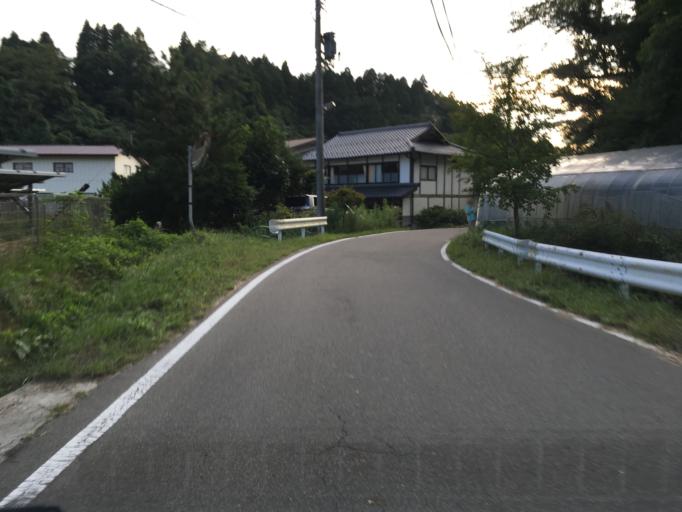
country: JP
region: Fukushima
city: Fukushima-shi
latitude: 37.6842
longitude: 140.5710
